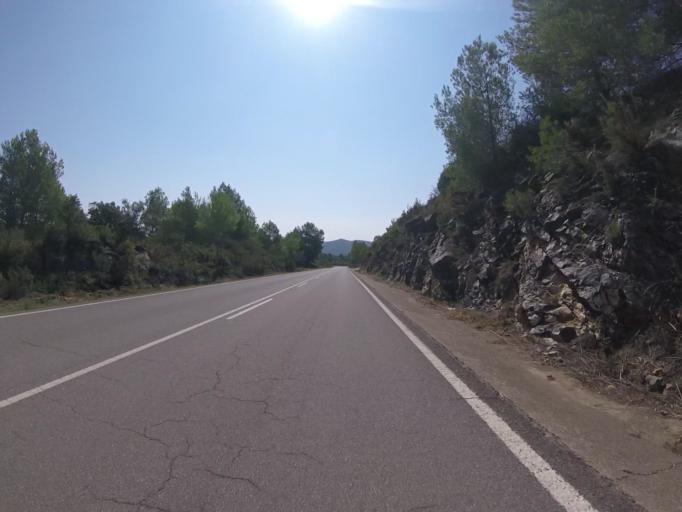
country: ES
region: Valencia
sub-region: Provincia de Castello
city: Adzaneta
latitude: 40.2365
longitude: -0.1832
